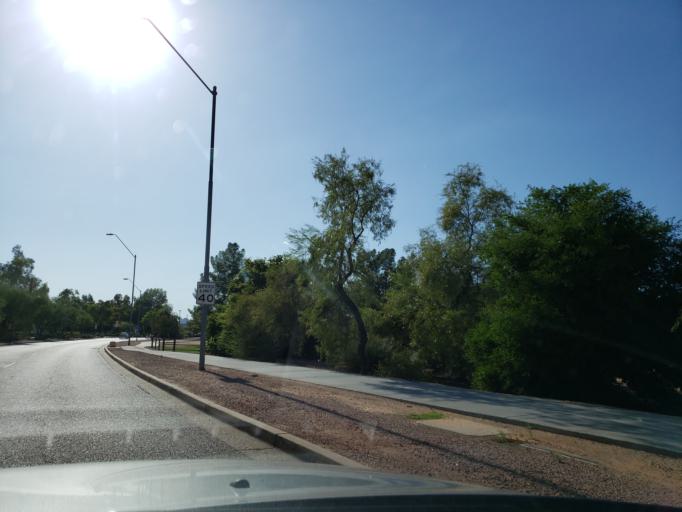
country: US
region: Arizona
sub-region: Maricopa County
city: Scottsdale
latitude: 33.5752
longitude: -111.8548
